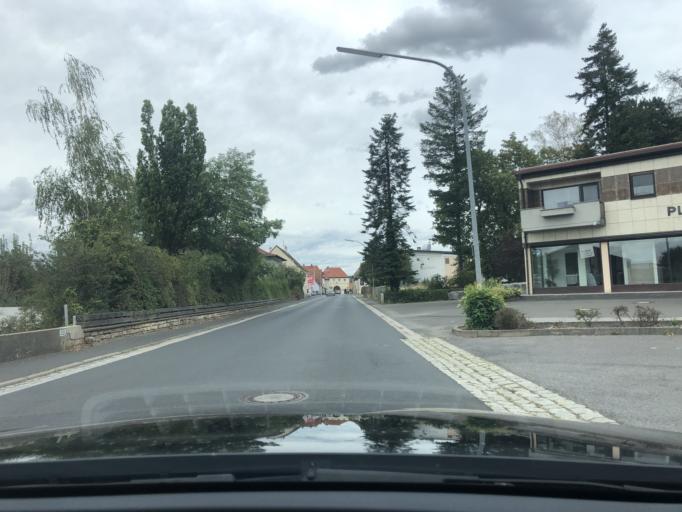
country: DE
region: Bavaria
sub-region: Regierungsbezirk Unterfranken
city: Hofheim in Unterfranken
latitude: 50.1326
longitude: 10.5217
